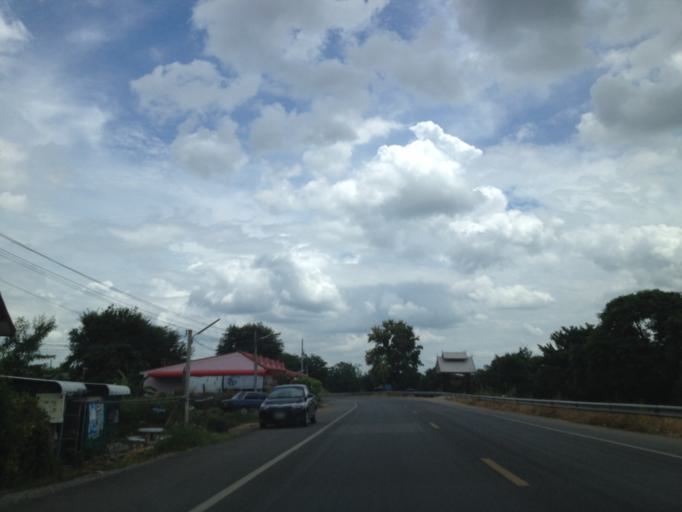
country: TH
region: Chiang Mai
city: San Pa Tong
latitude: 18.6337
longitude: 98.8620
